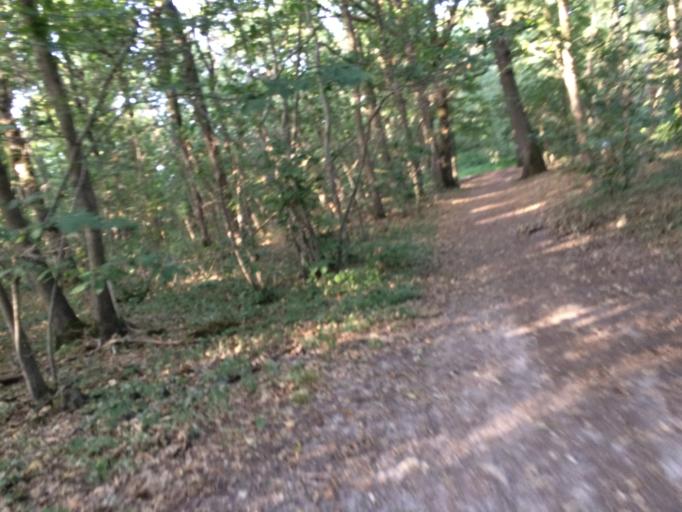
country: FR
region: Ile-de-France
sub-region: Departement de l'Essonne
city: Igny
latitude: 48.7504
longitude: 2.2399
